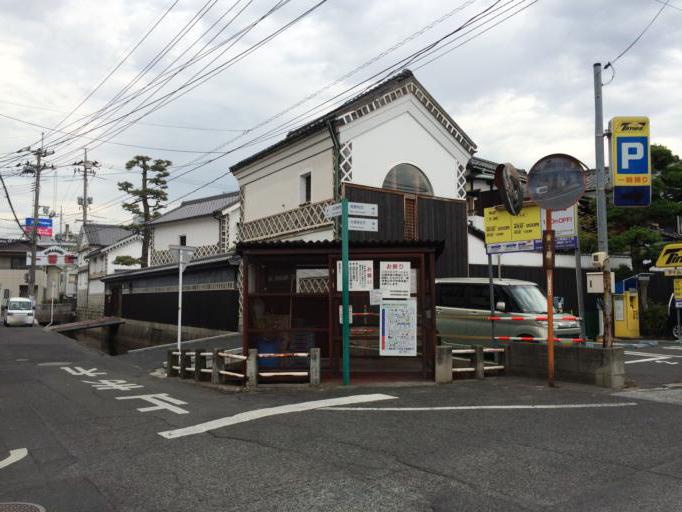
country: JP
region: Okayama
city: Kurashiki
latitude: 34.5971
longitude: 133.7667
